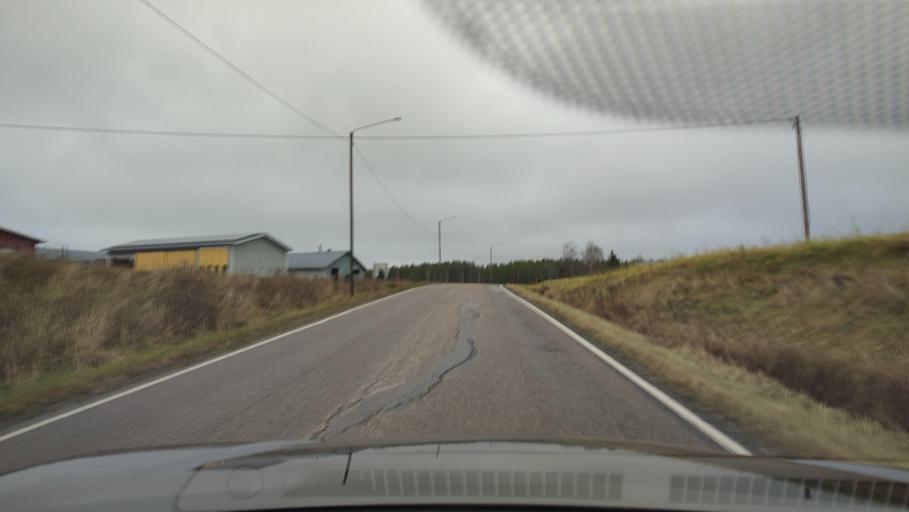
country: FI
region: Southern Ostrobothnia
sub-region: Suupohja
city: Isojoki
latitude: 62.1920
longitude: 21.9847
